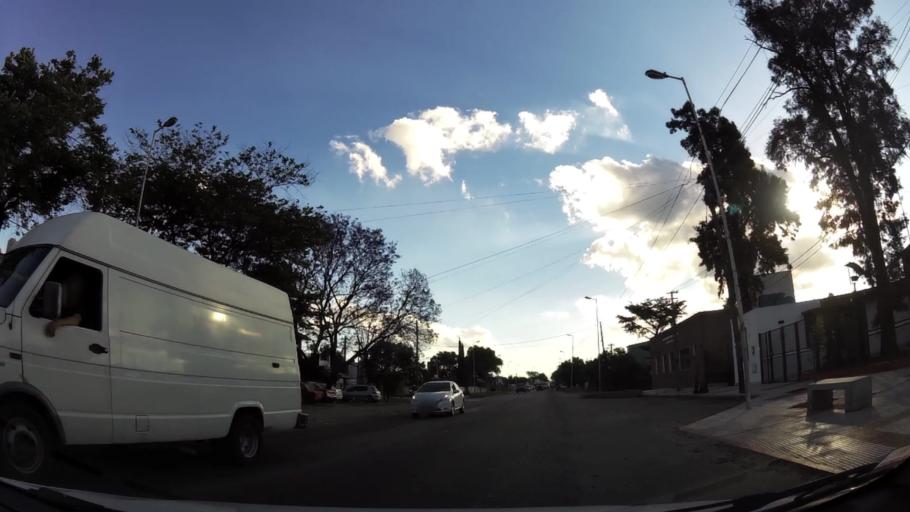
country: AR
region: Buenos Aires
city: Ituzaingo
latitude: -34.6942
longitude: -58.6392
